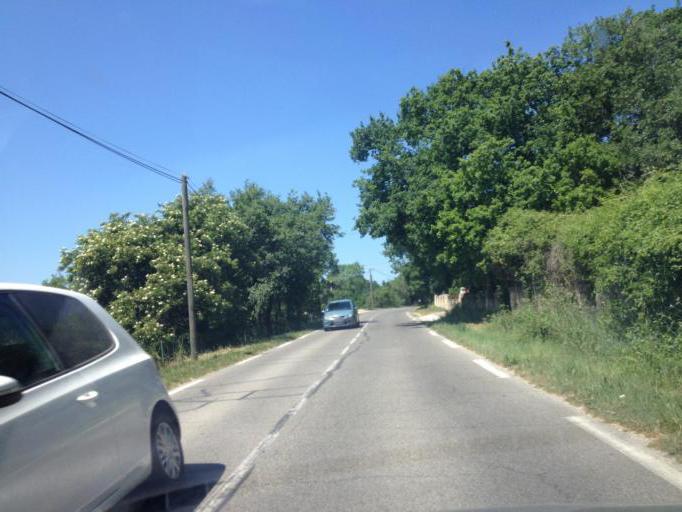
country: FR
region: Provence-Alpes-Cote d'Azur
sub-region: Departement du Vaucluse
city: Cadenet
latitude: 43.7419
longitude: 5.3634
